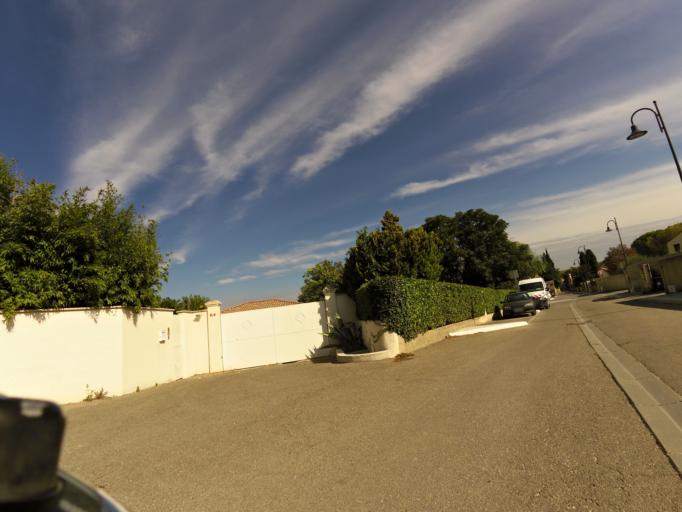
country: FR
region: Languedoc-Roussillon
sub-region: Departement du Gard
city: Aigues-Vives
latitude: 43.7395
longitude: 4.1741
